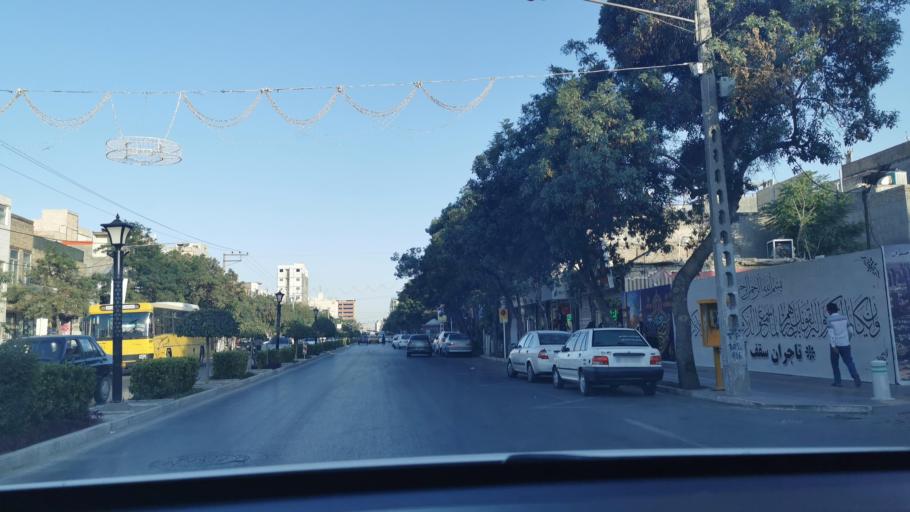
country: IR
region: Razavi Khorasan
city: Mashhad
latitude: 36.2963
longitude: 59.6431
